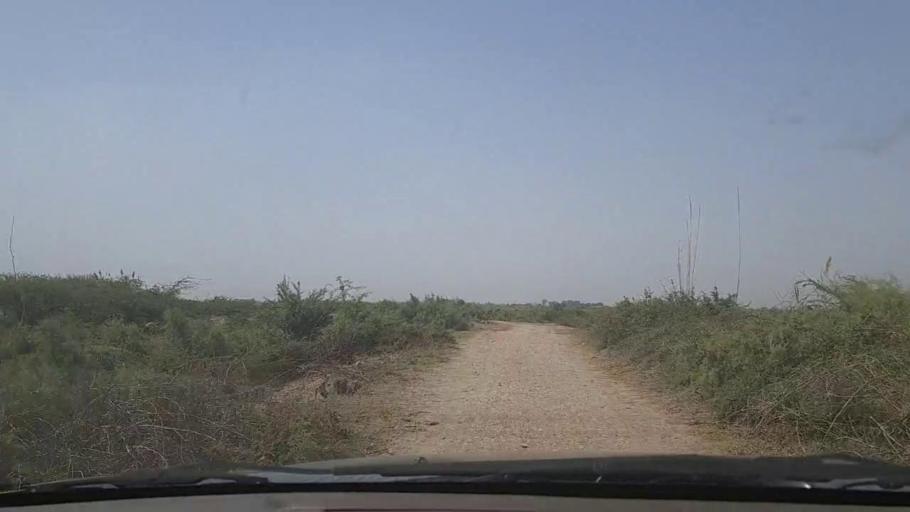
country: PK
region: Sindh
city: Keti Bandar
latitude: 24.2640
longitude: 67.6577
